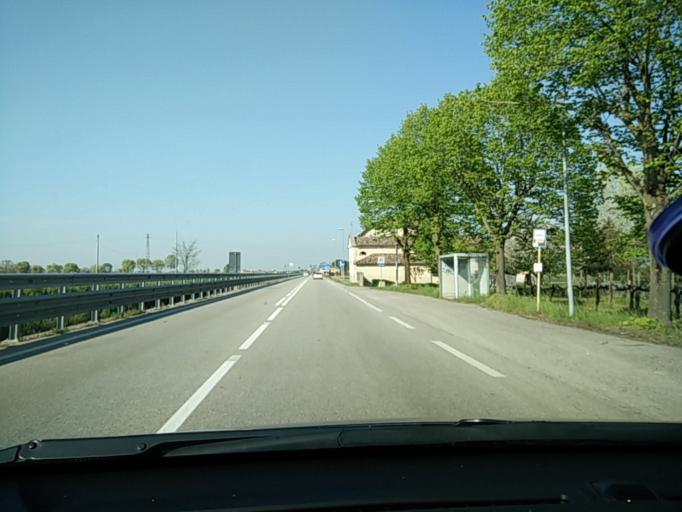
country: IT
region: Veneto
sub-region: Provincia di Venezia
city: Meolo
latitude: 45.6058
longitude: 12.4865
